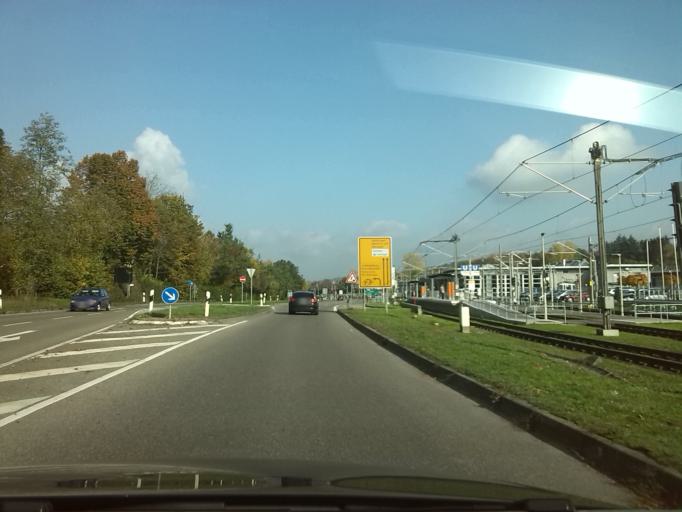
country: DE
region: Baden-Wuerttemberg
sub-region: Regierungsbezirk Stuttgart
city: Stuttgart Muehlhausen
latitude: 48.8565
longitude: 9.2480
